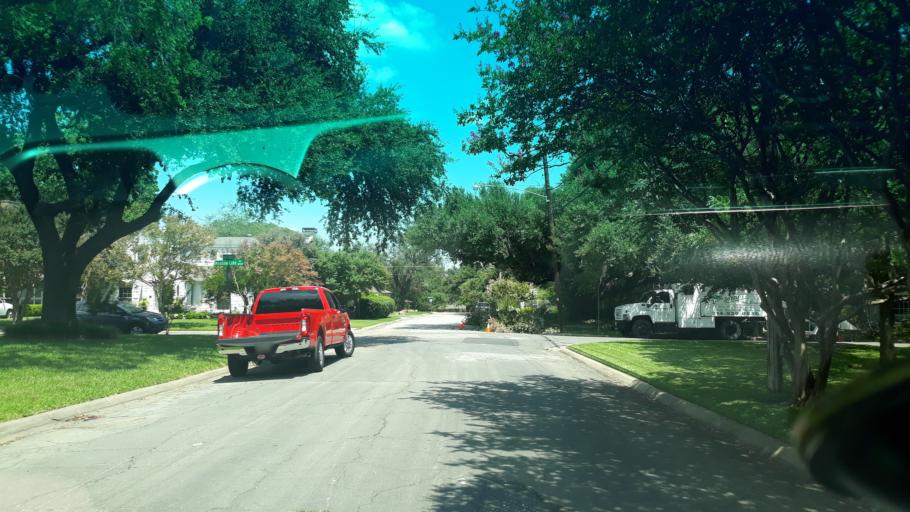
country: US
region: Texas
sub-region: Dallas County
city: Highland Park
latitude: 32.8234
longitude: -96.7385
